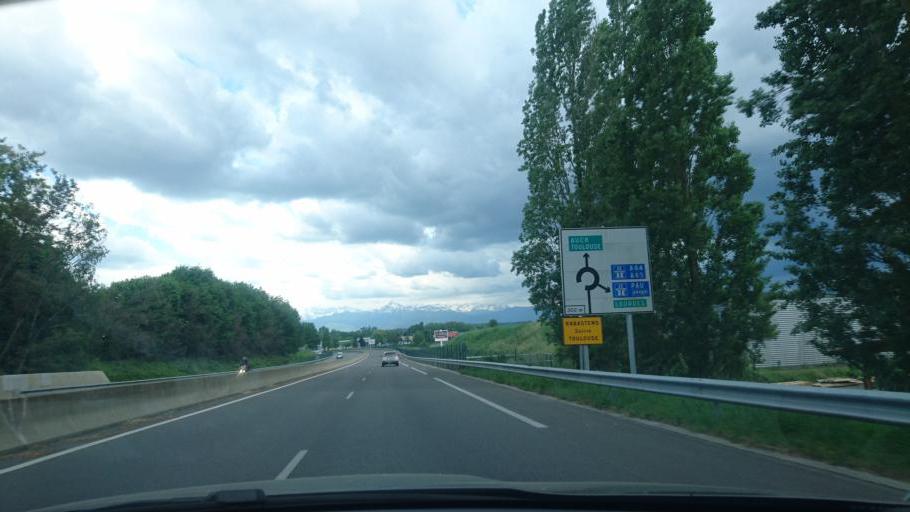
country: FR
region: Midi-Pyrenees
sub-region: Departement des Hautes-Pyrenees
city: Odos
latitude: 43.2266
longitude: 0.0450
